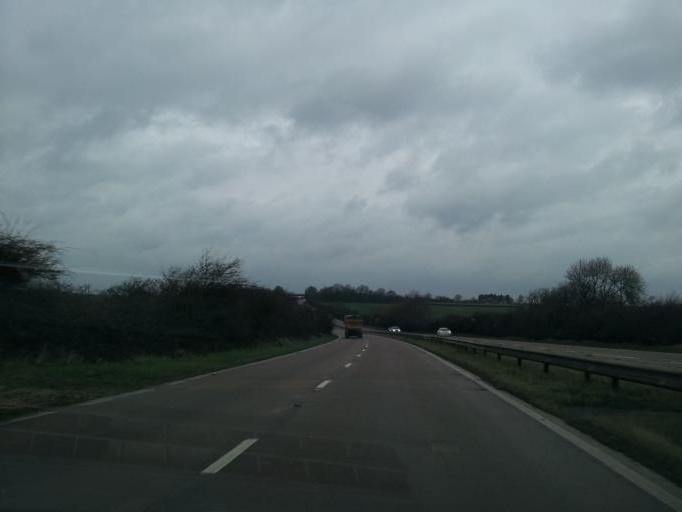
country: GB
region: England
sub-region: Leicestershire
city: Grimston
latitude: 52.8137
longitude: -1.0364
